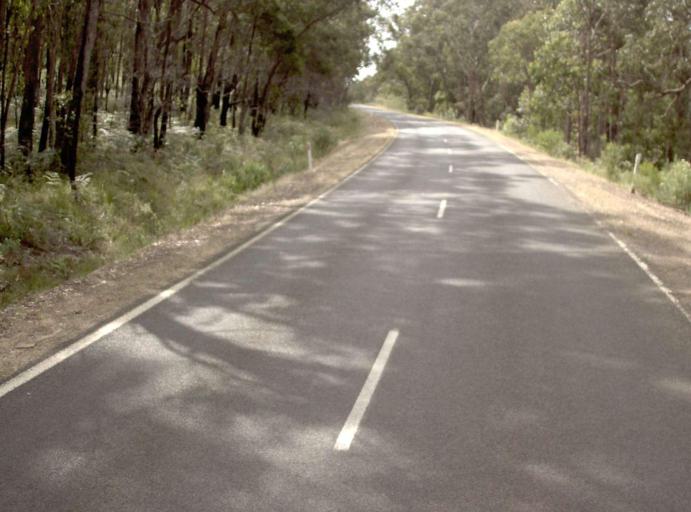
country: AU
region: Victoria
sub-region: Latrobe
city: Traralgon
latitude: -38.4024
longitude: 146.8231
